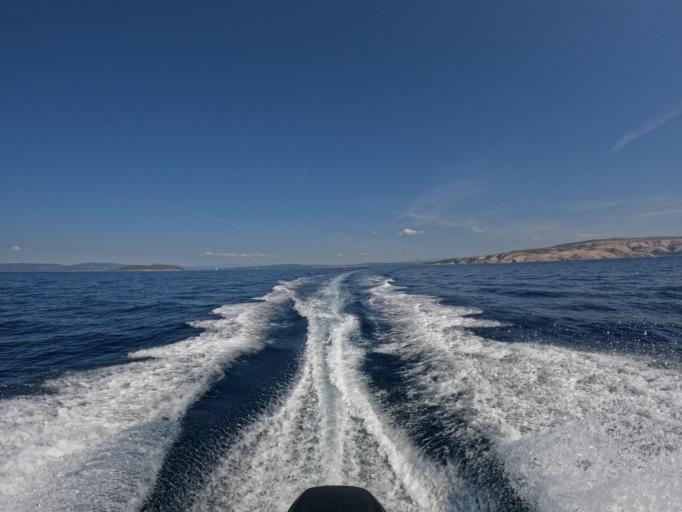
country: HR
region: Primorsko-Goranska
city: Punat
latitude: 44.9217
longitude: 14.6210
